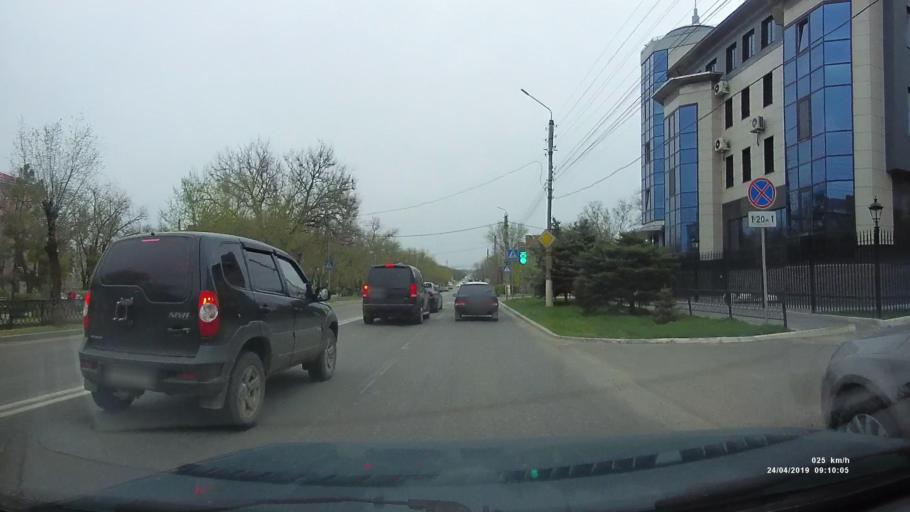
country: RU
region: Kalmykiya
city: Elista
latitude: 46.3095
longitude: 44.2760
